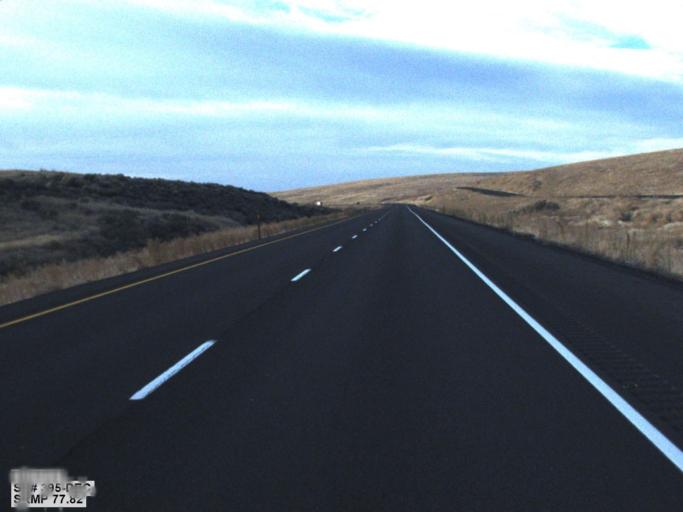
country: US
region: Washington
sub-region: Adams County
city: Ritzville
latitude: 46.9134
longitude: -118.6068
